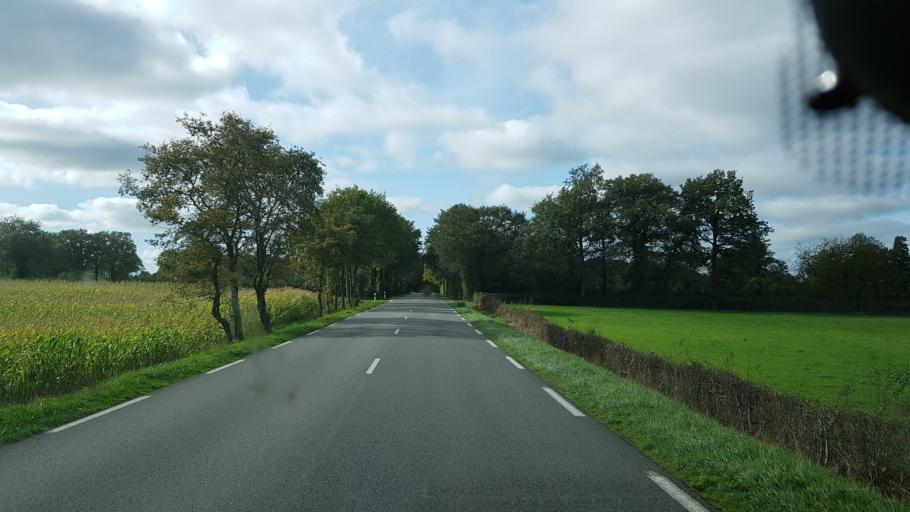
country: FR
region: Poitou-Charentes
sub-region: Departement de la Charente
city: Confolens
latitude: 46.0784
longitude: 0.7825
